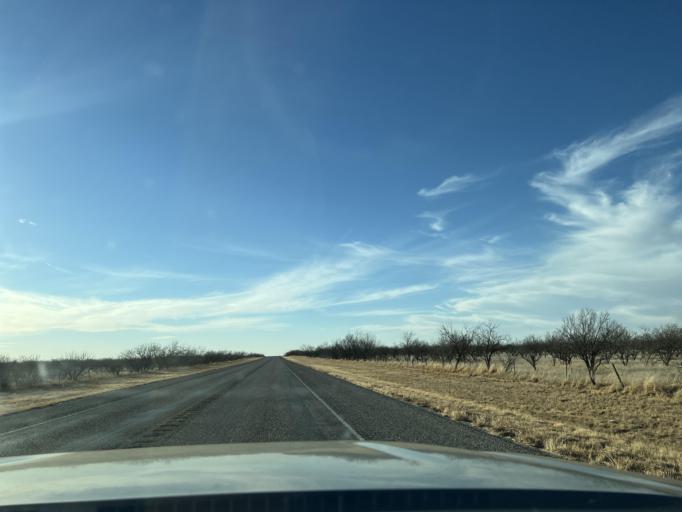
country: US
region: Texas
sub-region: Borden County
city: Gail
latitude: 32.7680
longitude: -101.3074
